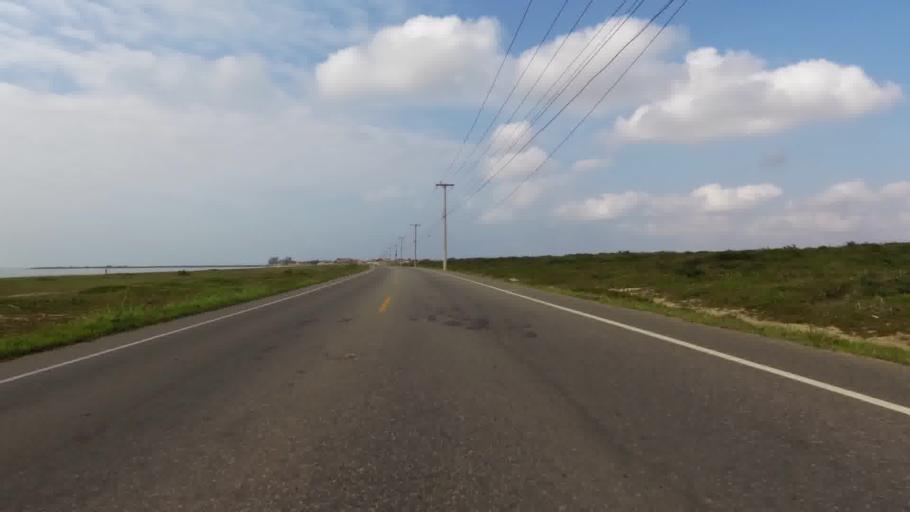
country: BR
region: Espirito Santo
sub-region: Itapemirim
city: Itapemirim
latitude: -20.9919
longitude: -40.8110
